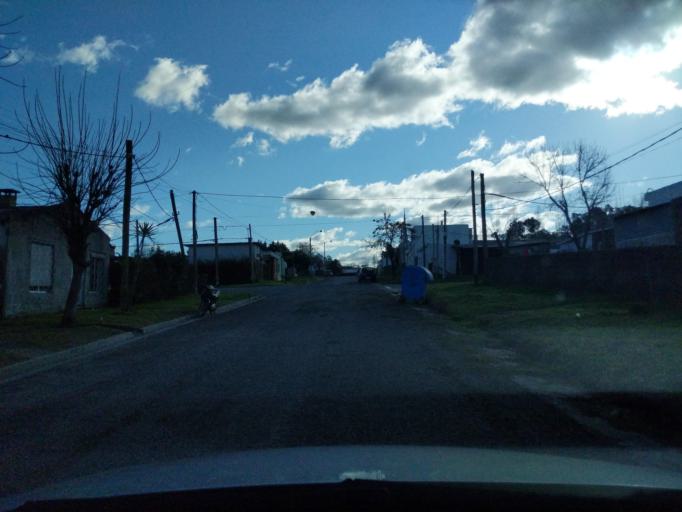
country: UY
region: Florida
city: Florida
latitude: -34.0874
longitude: -56.2104
